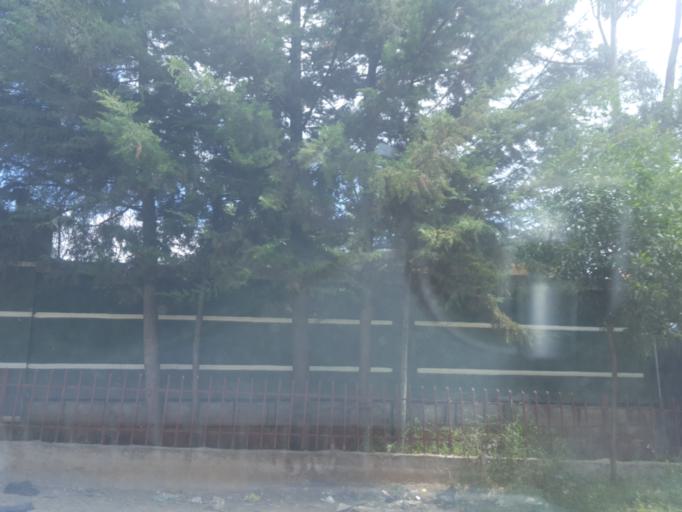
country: ET
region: Adis Abeba
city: Addis Ababa
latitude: 9.0650
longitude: 38.7432
